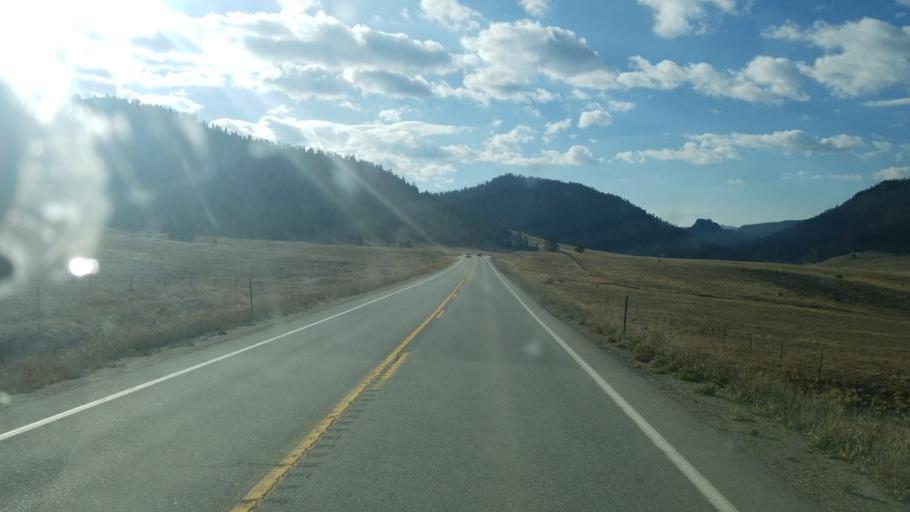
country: US
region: Colorado
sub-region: Chaffee County
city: Buena Vista
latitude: 38.8777
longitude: -105.9866
